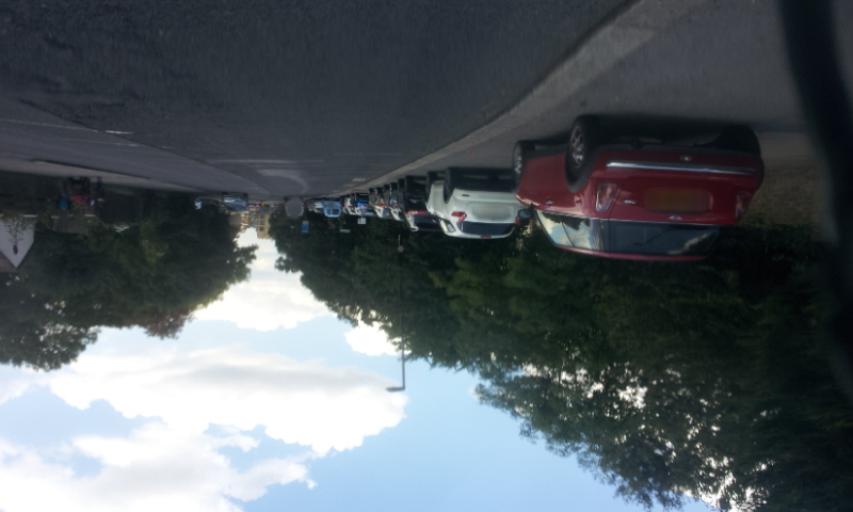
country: GB
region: England
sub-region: Greater London
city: Beckenham
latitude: 51.4282
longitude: -0.0599
